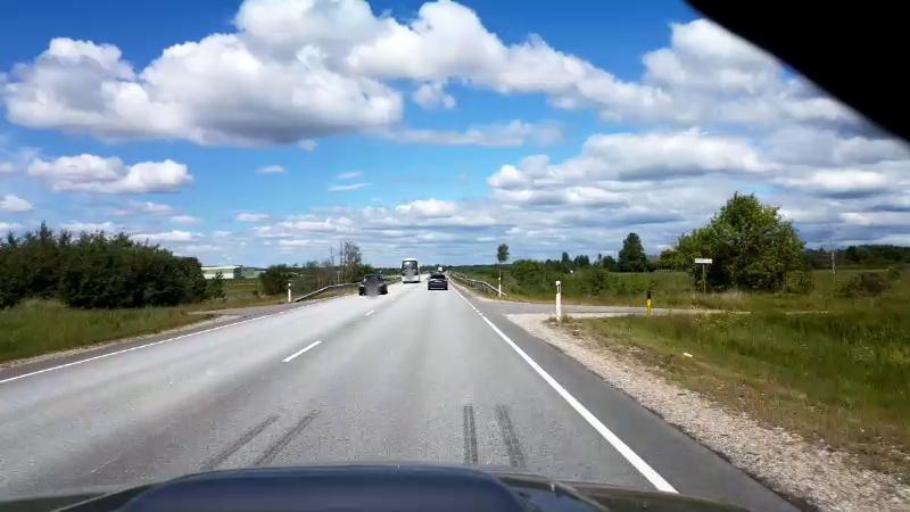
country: EE
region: Paernumaa
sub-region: Sauga vald
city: Sauga
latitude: 58.4804
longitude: 24.5279
